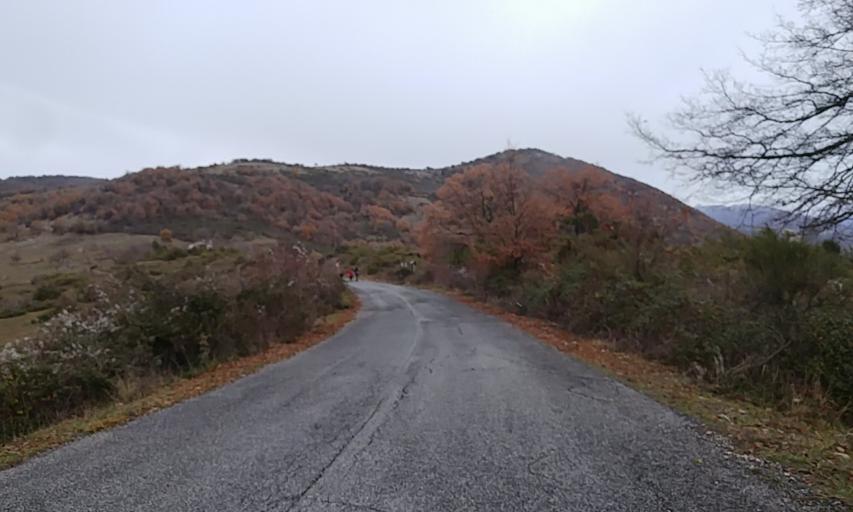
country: IT
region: Latium
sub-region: Provincia di Rieti
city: Orvinio
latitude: 42.1358
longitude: 12.9059
